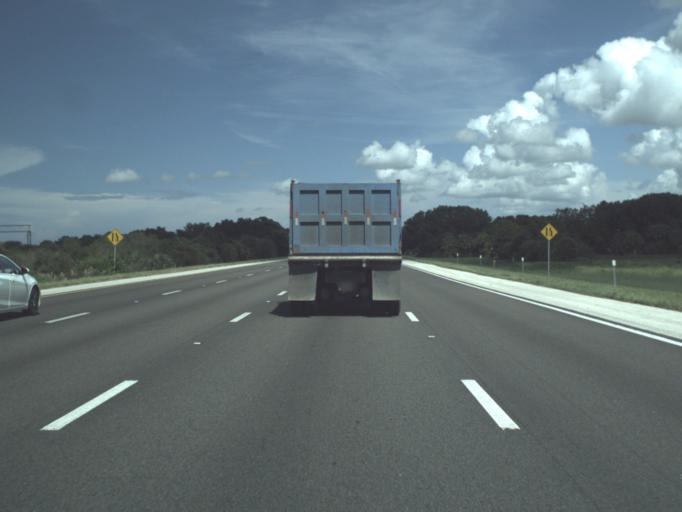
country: US
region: Florida
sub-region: Sarasota County
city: Osprey
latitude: 27.2059
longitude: -82.4416
